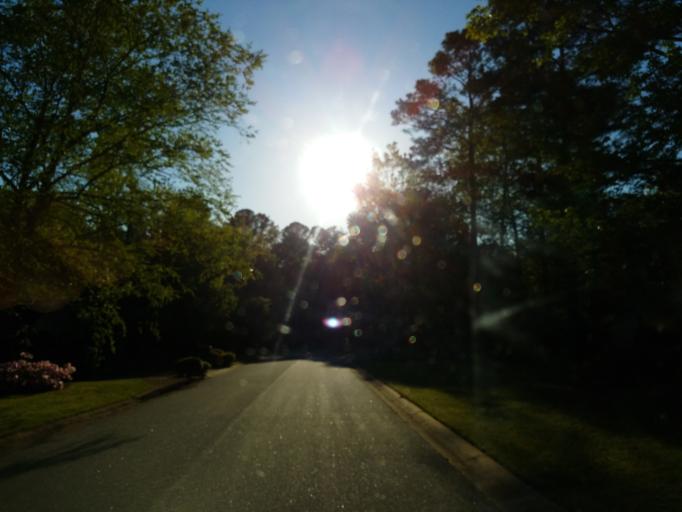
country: US
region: Georgia
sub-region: Cobb County
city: Powder Springs
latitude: 33.9175
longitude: -84.6415
